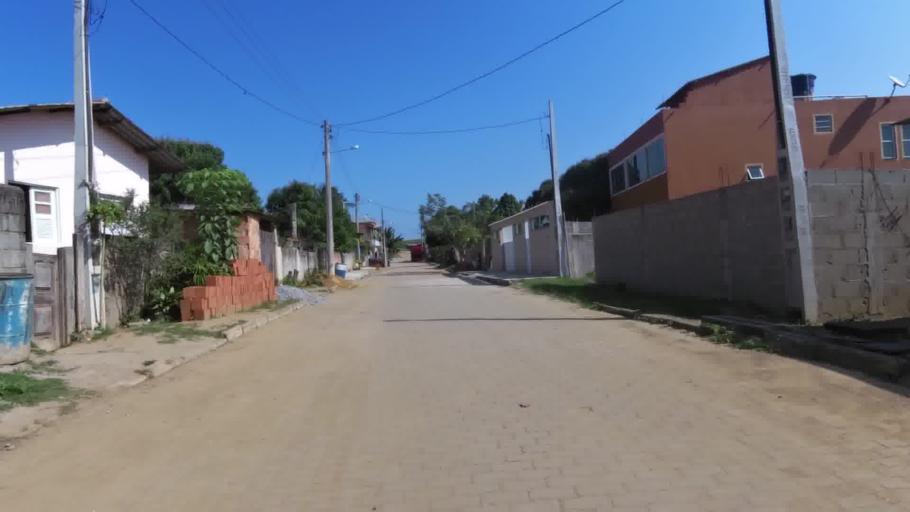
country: BR
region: Espirito Santo
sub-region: Piuma
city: Piuma
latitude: -20.8105
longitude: -40.7387
